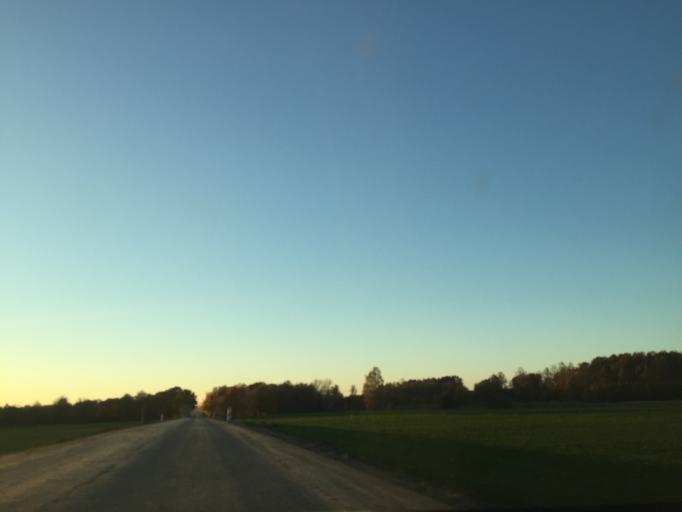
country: LT
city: Vieksniai
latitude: 56.4046
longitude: 22.5204
